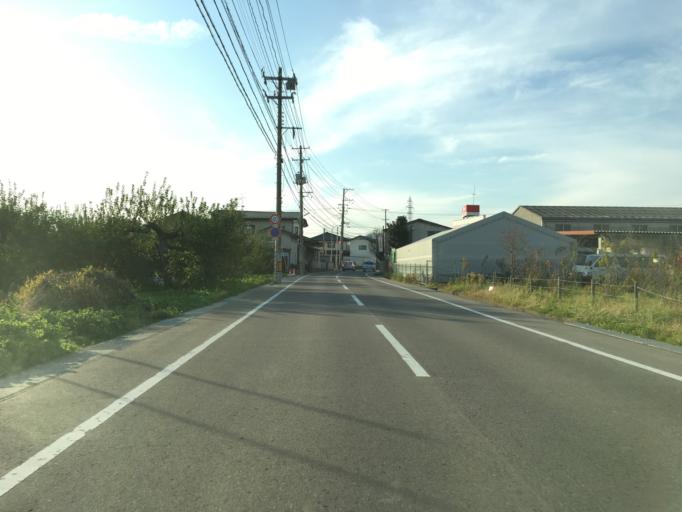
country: JP
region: Fukushima
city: Fukushima-shi
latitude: 37.8024
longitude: 140.4744
